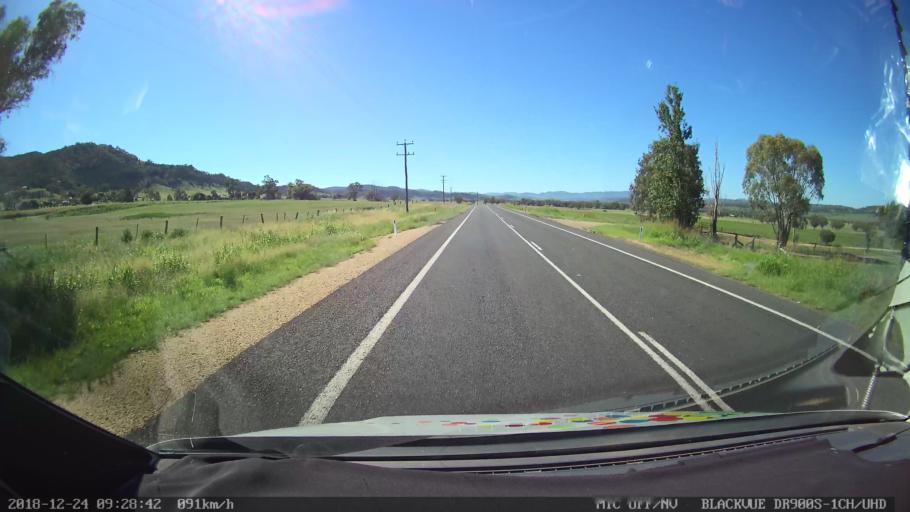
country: AU
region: New South Wales
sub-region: Liverpool Plains
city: Quirindi
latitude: -31.5407
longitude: 150.6909
